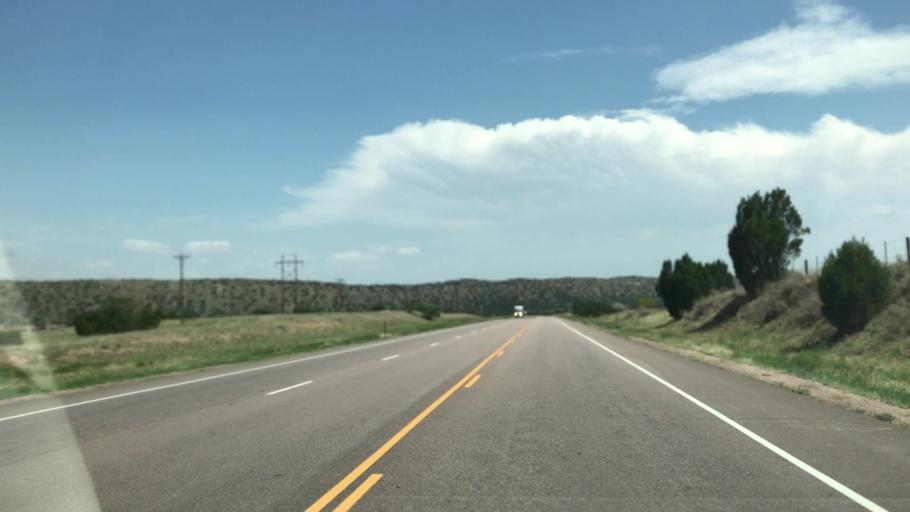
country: US
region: Colorado
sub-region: Fremont County
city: Canon City
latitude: 38.4865
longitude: -105.2747
